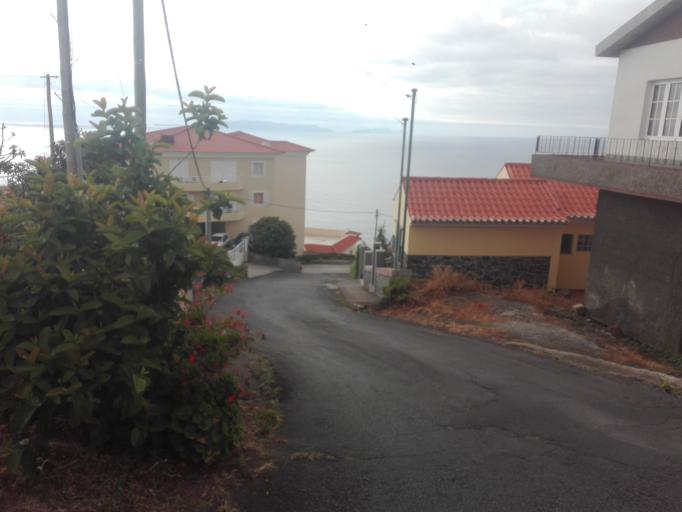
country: PT
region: Madeira
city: Canico
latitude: 32.6523
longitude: -16.8272
